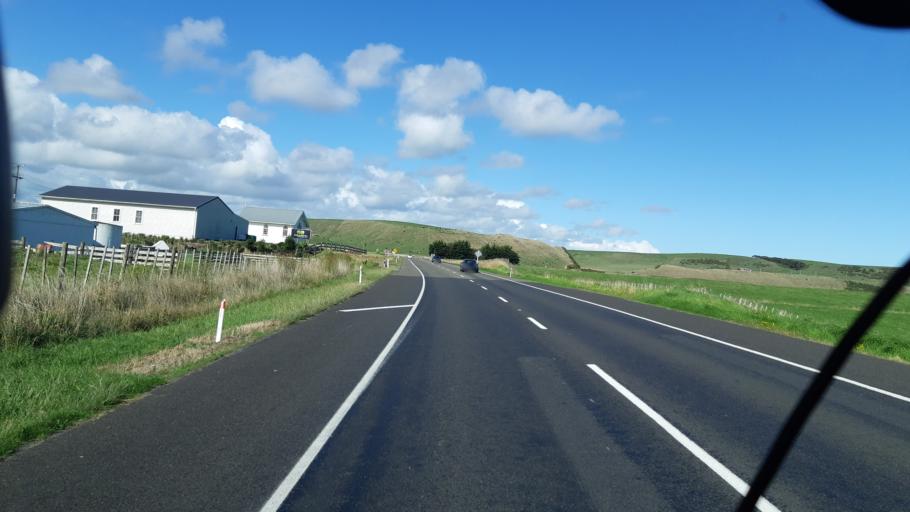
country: NZ
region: Manawatu-Wanganui
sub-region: Wanganui District
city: Wanganui
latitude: -40.0081
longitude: 175.1681
